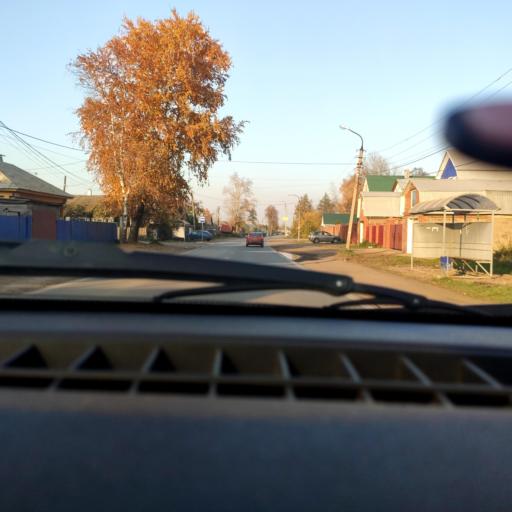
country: RU
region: Bashkortostan
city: Ufa
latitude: 54.8160
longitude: 56.1663
